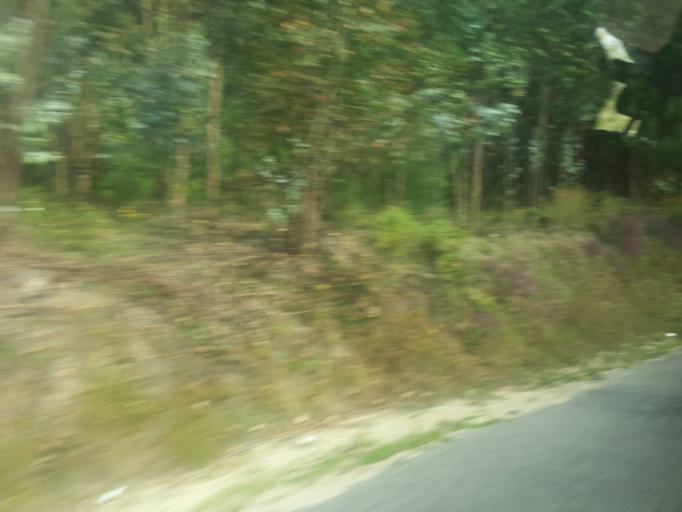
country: PT
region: Porto
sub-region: Marco de Canaveses
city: Marco de Canavezes
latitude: 41.1707
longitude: -8.1933
